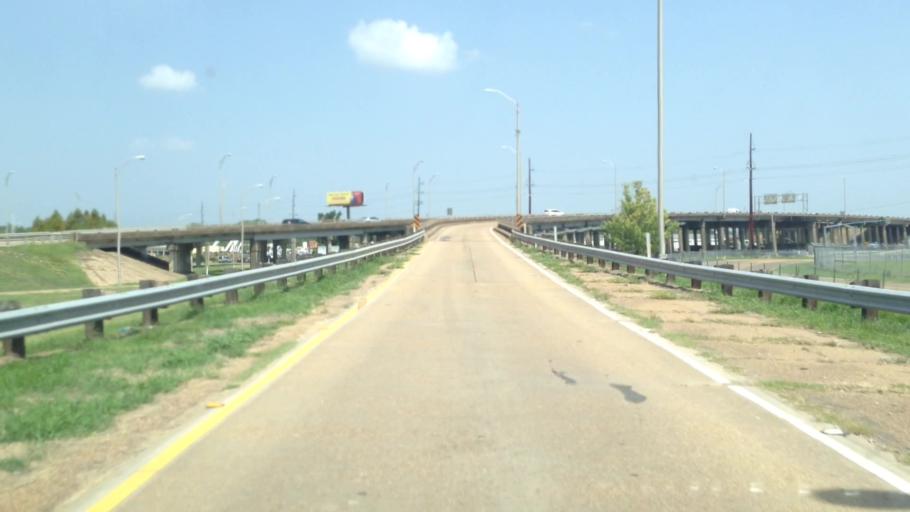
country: US
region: Louisiana
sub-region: Ouachita Parish
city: Monroe
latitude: 32.5003
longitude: -92.0815
